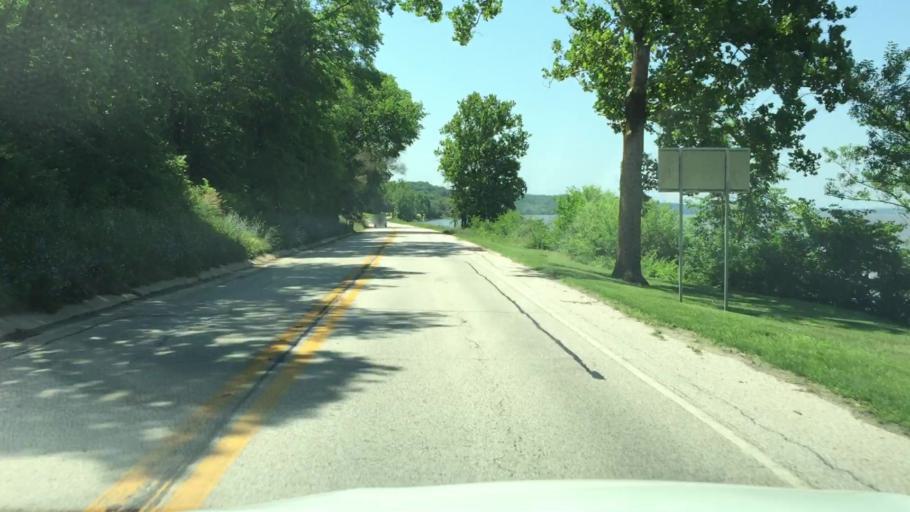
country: US
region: Illinois
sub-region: Hancock County
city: Nauvoo
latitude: 40.5045
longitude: -91.3565
